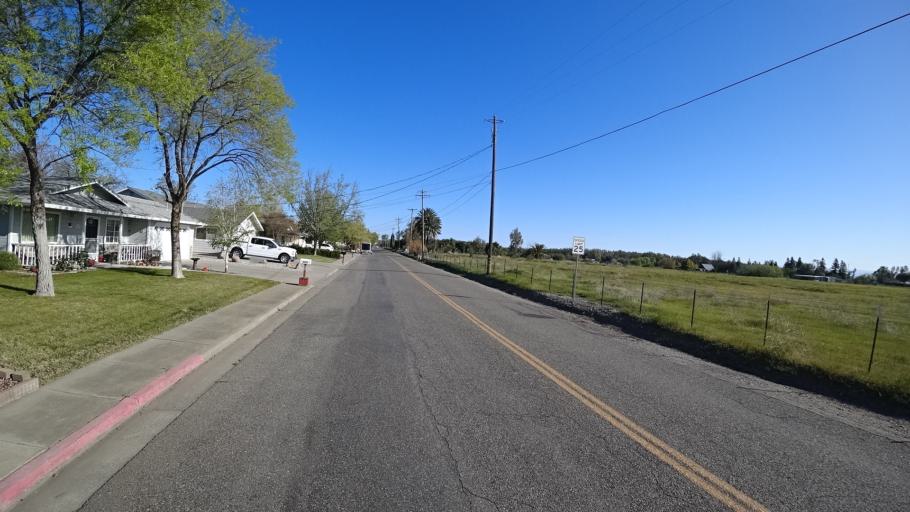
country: US
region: California
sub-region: Glenn County
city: Orland
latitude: 39.7570
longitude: -122.2203
